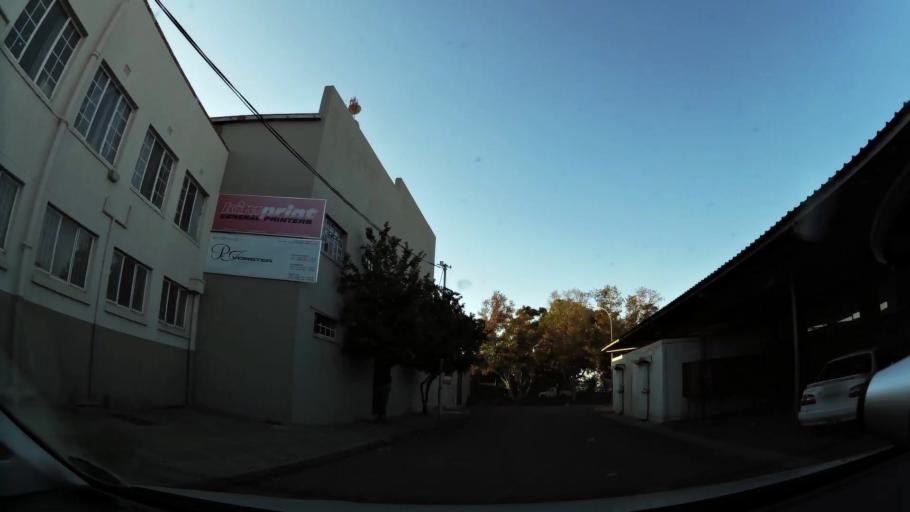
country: ZA
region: Northern Cape
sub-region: Frances Baard District Municipality
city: Kimberley
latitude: -28.7370
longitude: 24.7709
